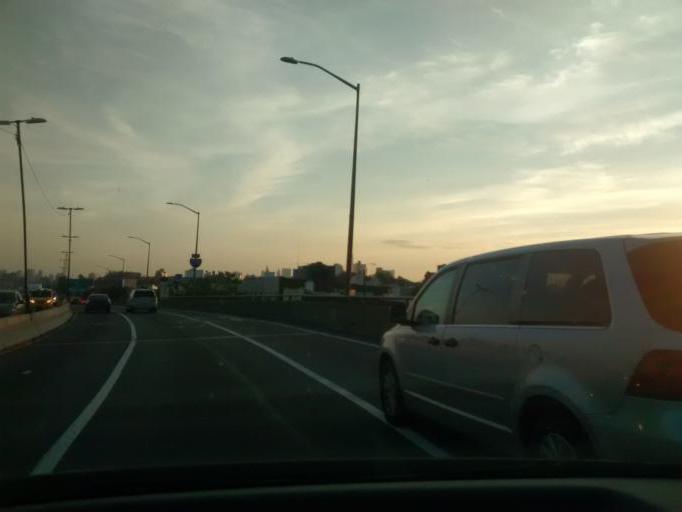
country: US
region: New York
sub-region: Queens County
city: Long Island City
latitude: 40.7244
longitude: -73.9372
